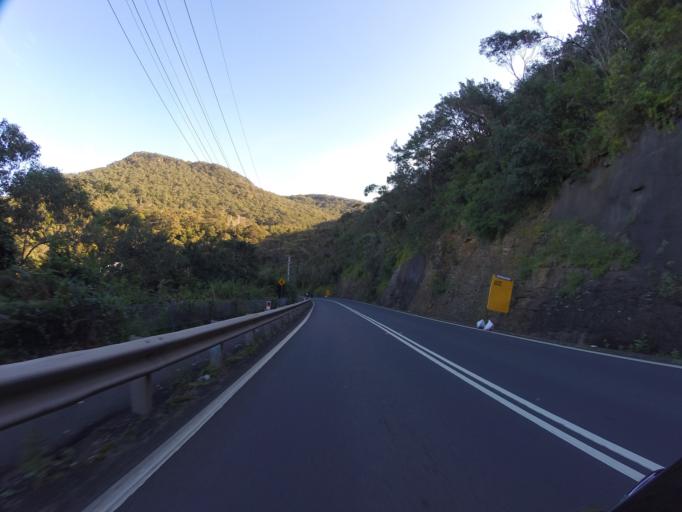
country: AU
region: New South Wales
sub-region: Wollongong
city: Helensburgh
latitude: -34.2441
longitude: 150.9747
